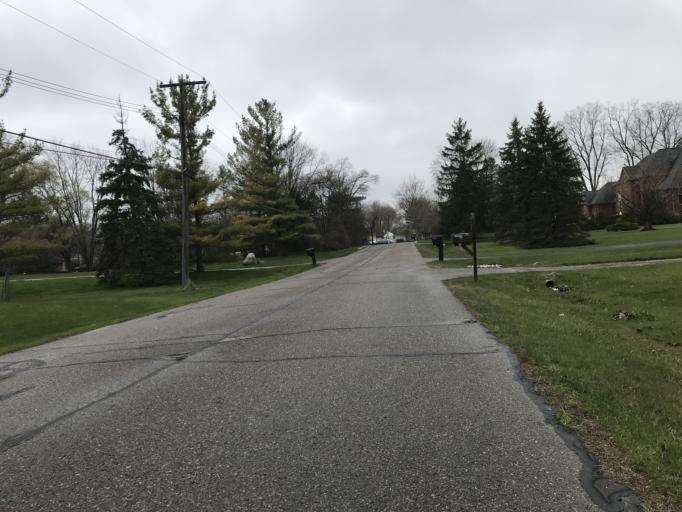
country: US
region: Michigan
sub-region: Oakland County
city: Farmington
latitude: 42.4685
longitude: -83.3410
